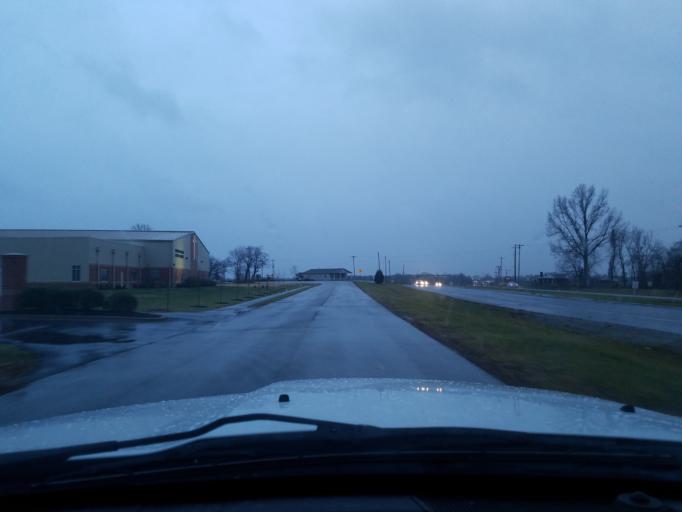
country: US
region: Indiana
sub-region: Clark County
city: Oak Park
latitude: 38.3394
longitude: -85.7062
